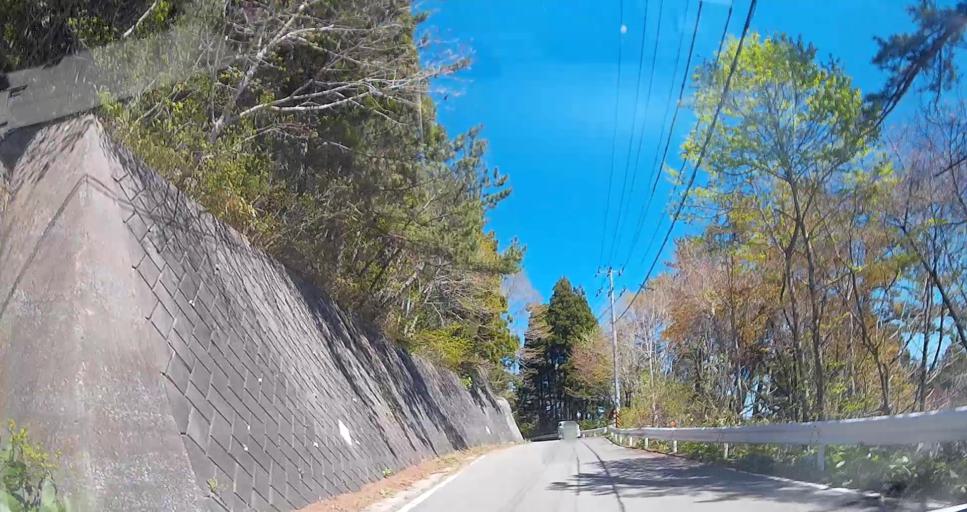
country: JP
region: Aomori
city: Mutsu
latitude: 41.1191
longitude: 141.3917
